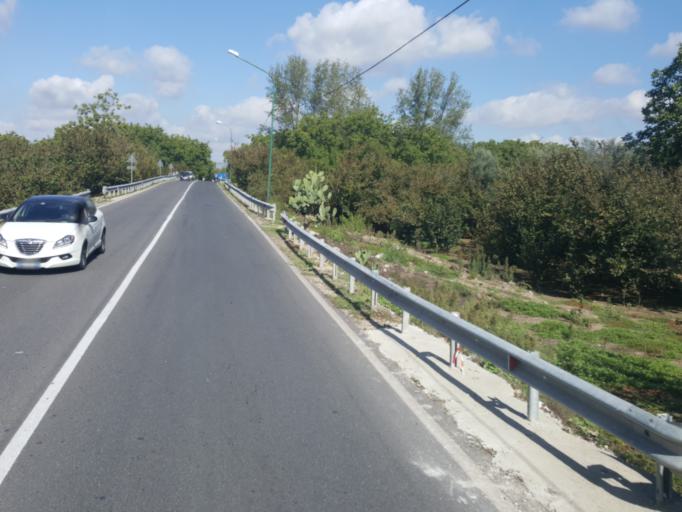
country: IT
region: Campania
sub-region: Provincia di Napoli
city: Nola
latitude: 40.9227
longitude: 14.5123
